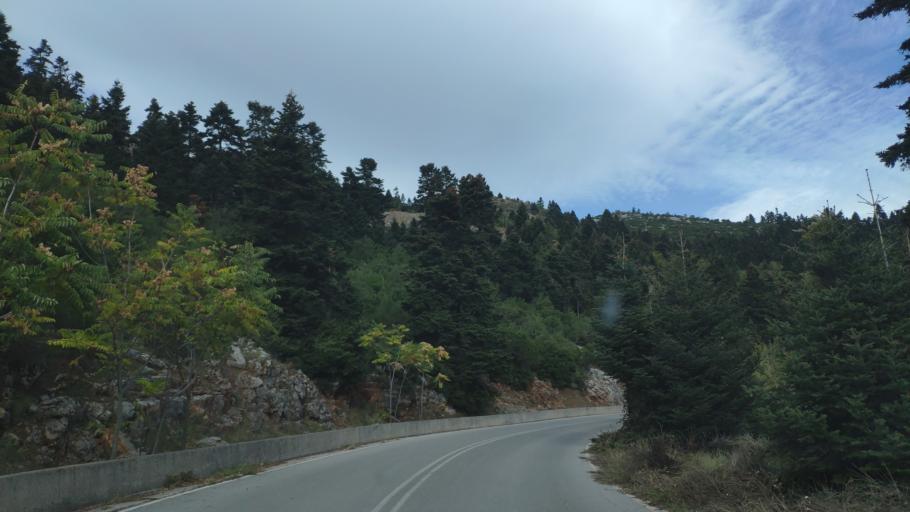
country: GR
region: Central Greece
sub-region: Nomos Fokidos
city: Amfissa
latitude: 38.6386
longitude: 22.3824
